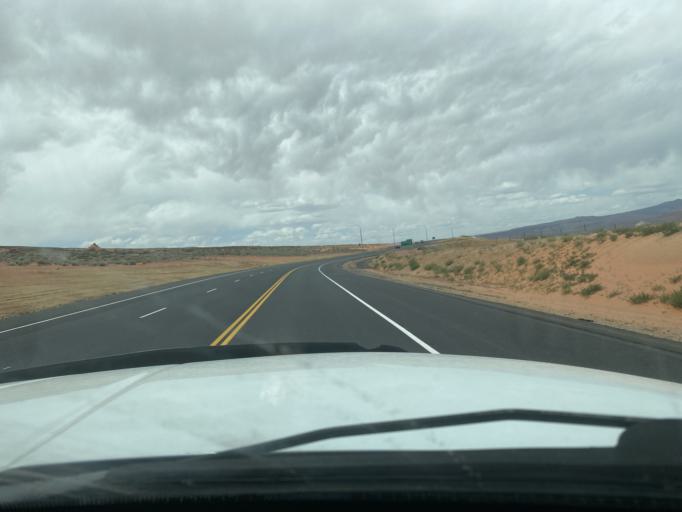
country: US
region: Utah
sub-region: Washington County
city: Washington
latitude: 37.1032
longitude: -113.3906
